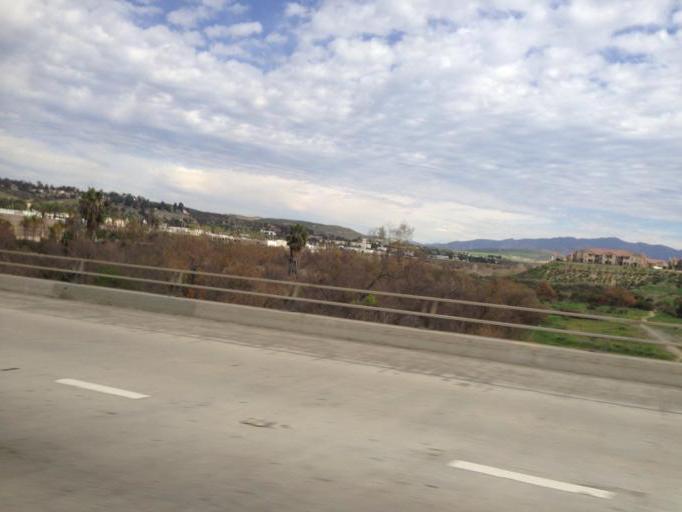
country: US
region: California
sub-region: San Diego County
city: Bonita
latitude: 32.5904
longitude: -117.0362
